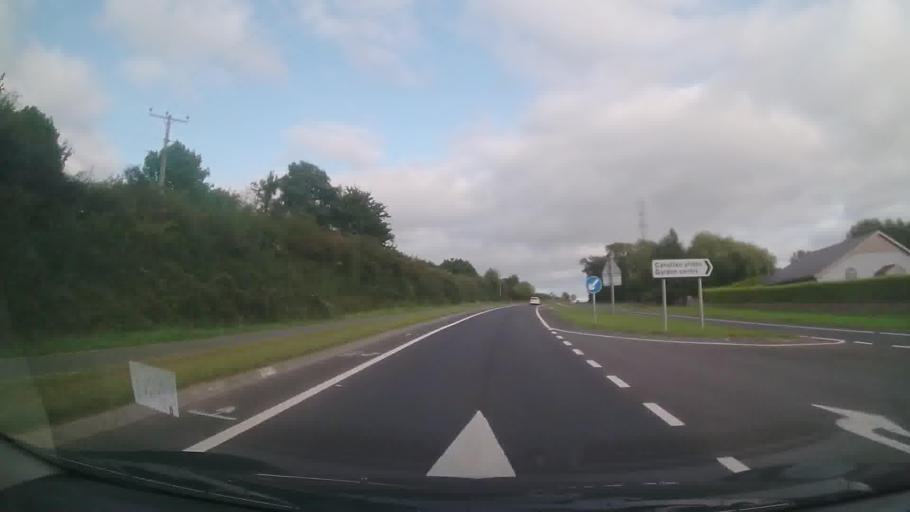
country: GB
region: Wales
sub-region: Pembrokeshire
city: Pembroke
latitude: 51.6898
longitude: -4.8949
